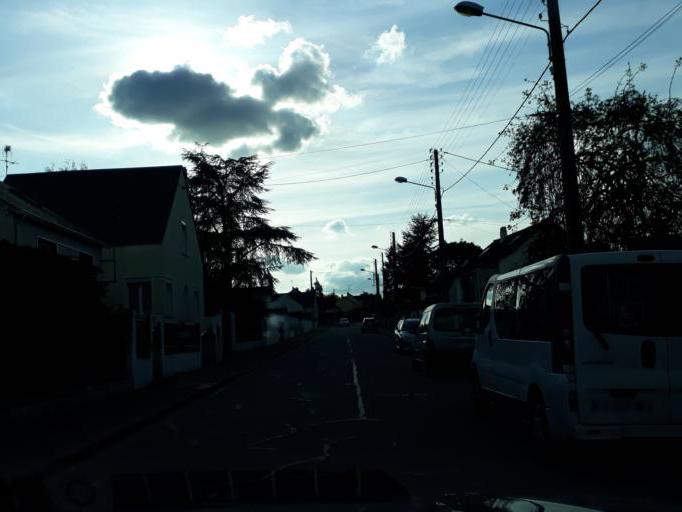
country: FR
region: Centre
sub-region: Departement du Loiret
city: Saint-Jean-de-la-Ruelle
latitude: 47.9195
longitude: 1.8803
